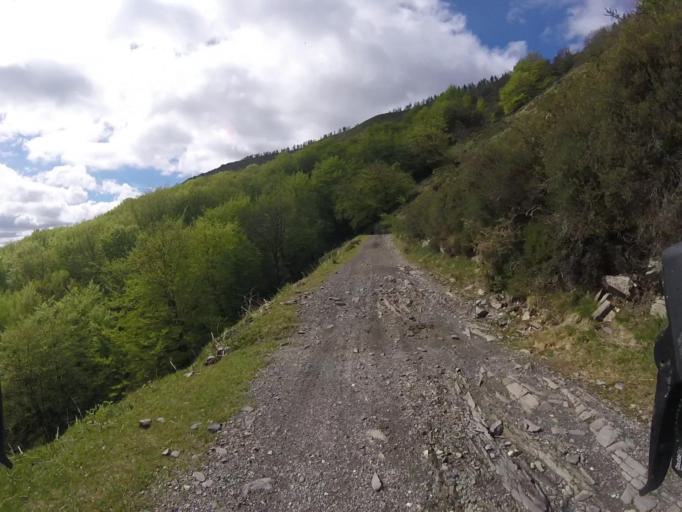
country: ES
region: Navarre
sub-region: Provincia de Navarra
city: Arano
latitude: 43.1739
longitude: -1.9186
